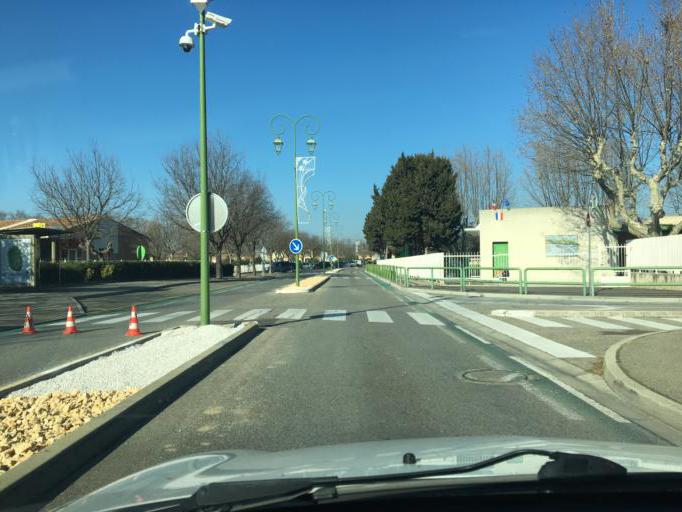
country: FR
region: Provence-Alpes-Cote d'Azur
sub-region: Departement des Bouches-du-Rhone
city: Mallemort
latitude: 43.7243
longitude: 5.1799
